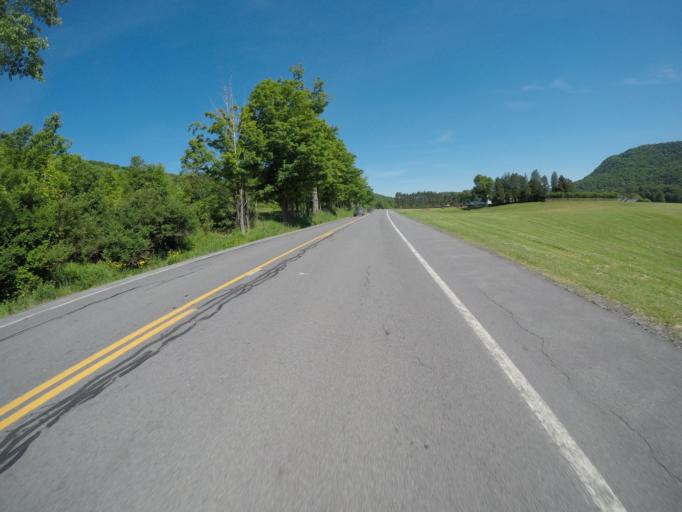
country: US
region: New York
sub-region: Delaware County
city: Delhi
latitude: 42.2231
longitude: -74.9688
